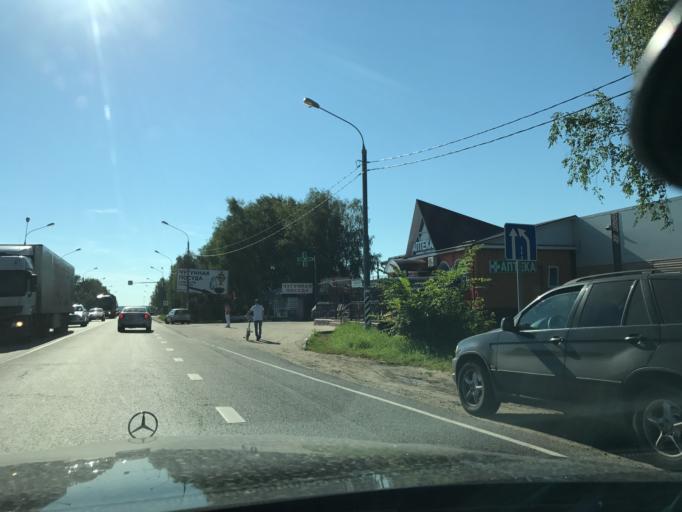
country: RU
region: Moskovskaya
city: Noginsk-9
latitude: 56.1089
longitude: 38.6212
